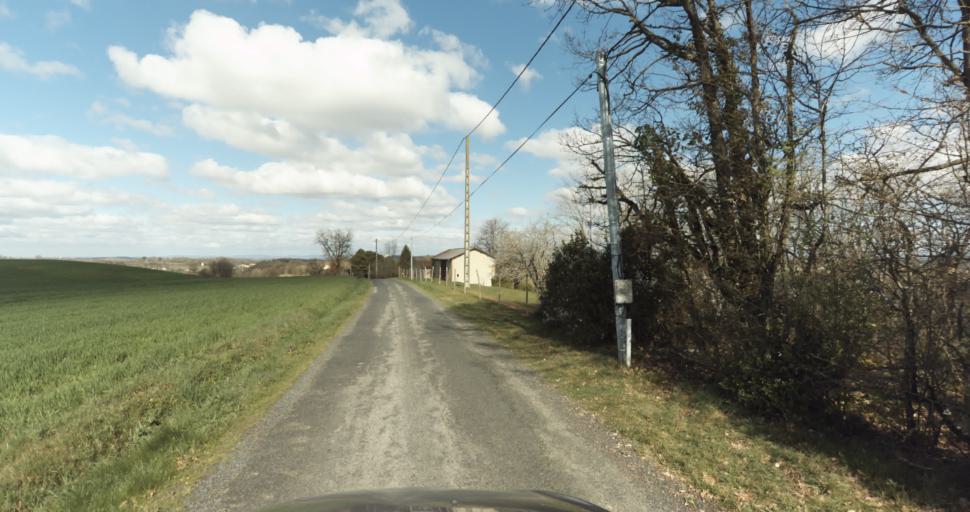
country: FR
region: Midi-Pyrenees
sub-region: Departement du Tarn
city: Puygouzon
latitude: 43.8654
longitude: 2.1762
